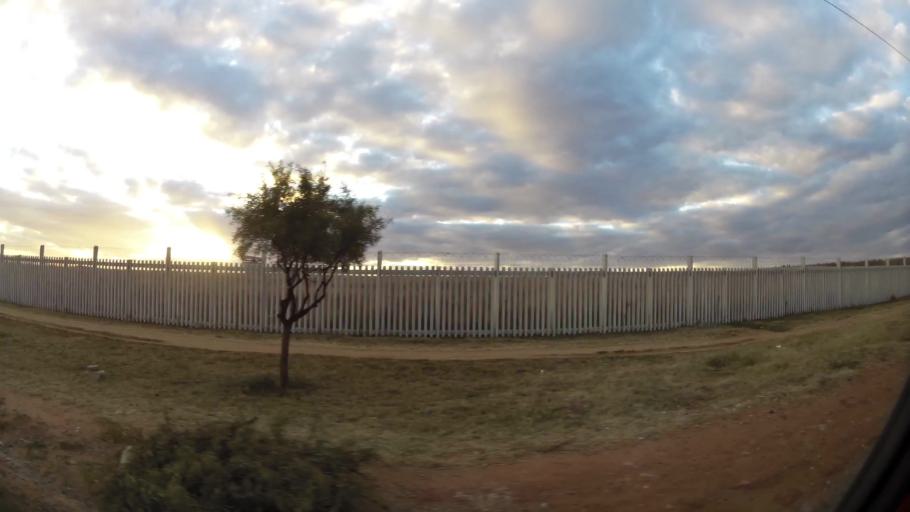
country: ZA
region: Gauteng
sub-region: City of Johannesburg Metropolitan Municipality
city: Midrand
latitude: -25.9963
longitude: 28.1440
